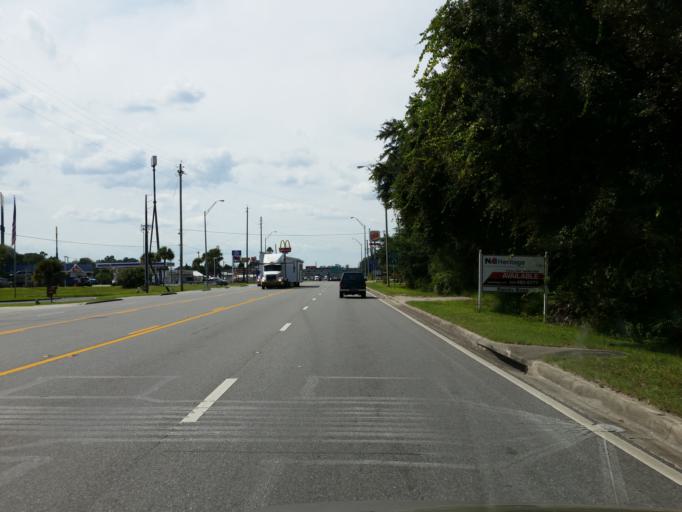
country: US
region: Florida
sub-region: Sumter County
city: Wildwood
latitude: 28.8722
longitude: -82.0877
